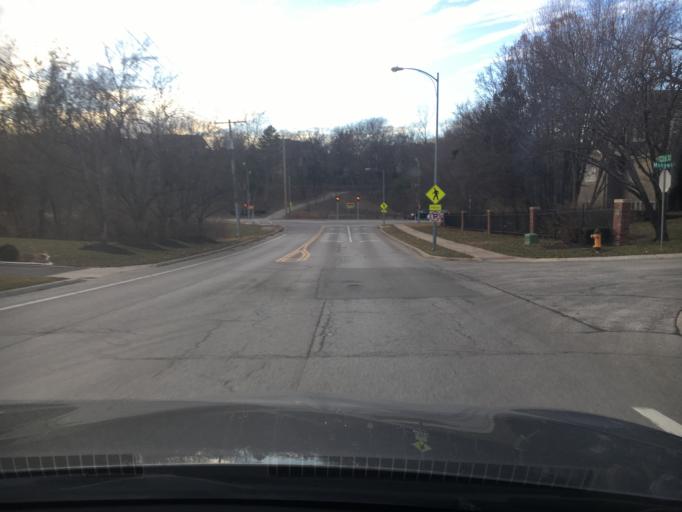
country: US
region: Kansas
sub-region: Johnson County
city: Leawood
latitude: 38.9056
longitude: -94.6293
